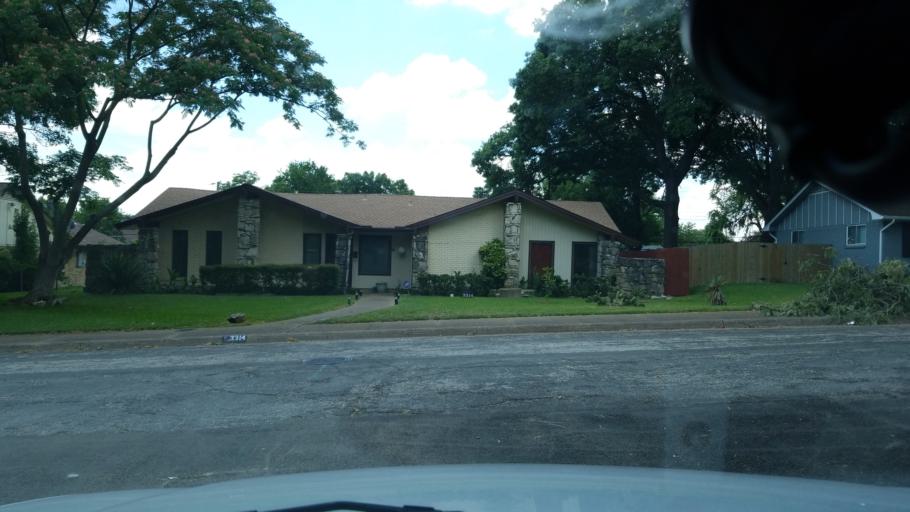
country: US
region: Texas
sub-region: Dallas County
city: Cockrell Hill
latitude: 32.6942
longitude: -96.8749
